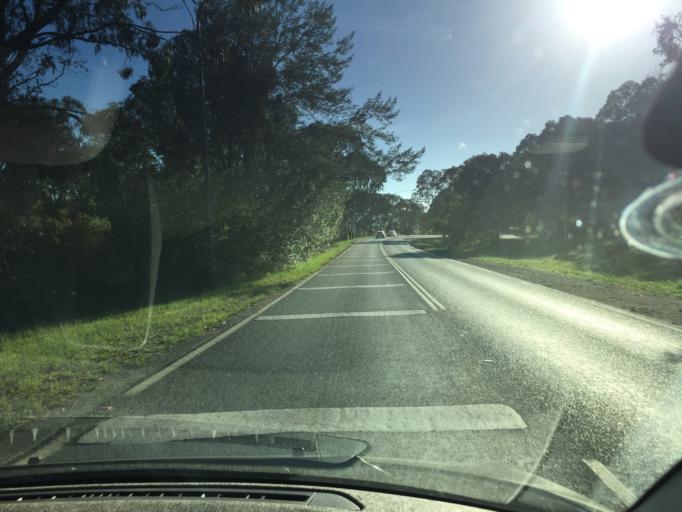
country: AU
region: Australian Capital Territory
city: Kaleen
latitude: -35.2316
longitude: 149.1217
